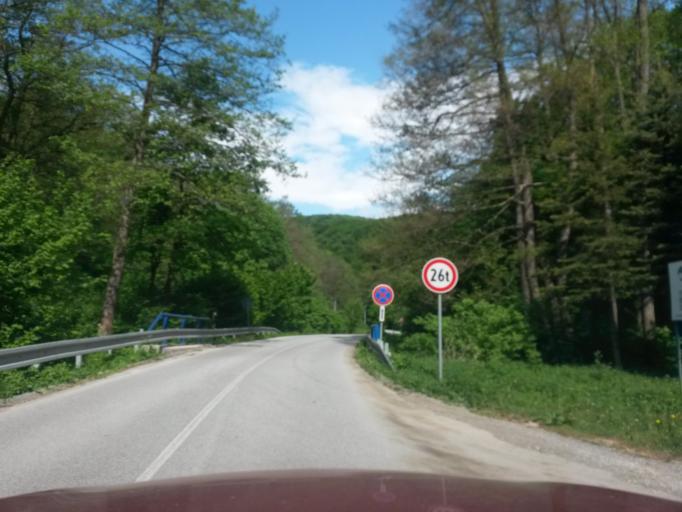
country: SK
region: Kosicky
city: Moldava nad Bodvou
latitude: 48.7256
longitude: 21.0687
